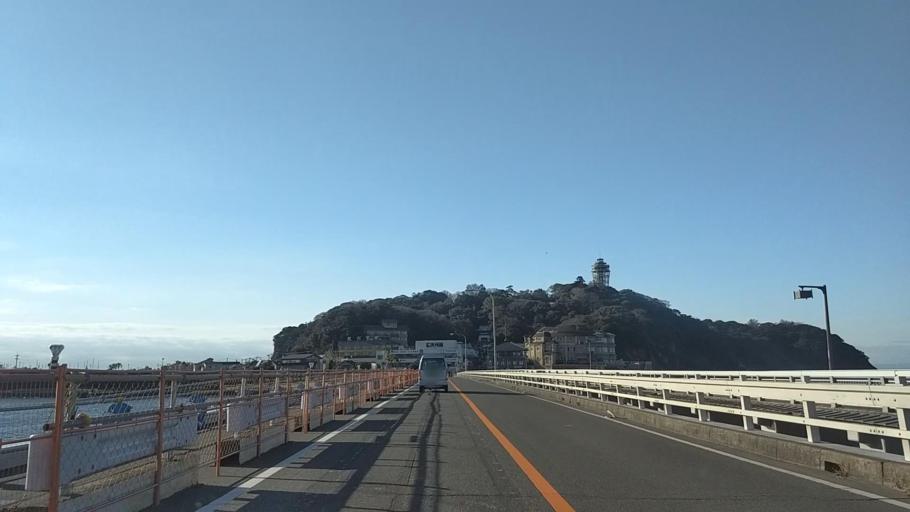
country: JP
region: Kanagawa
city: Fujisawa
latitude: 35.3047
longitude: 139.4825
